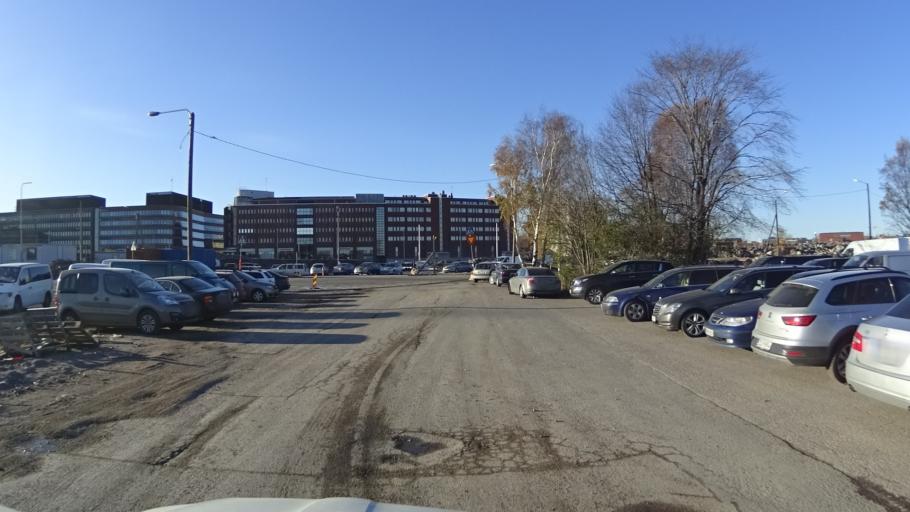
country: FI
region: Uusimaa
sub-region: Helsinki
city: Helsinki
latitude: 60.1907
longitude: 24.9822
